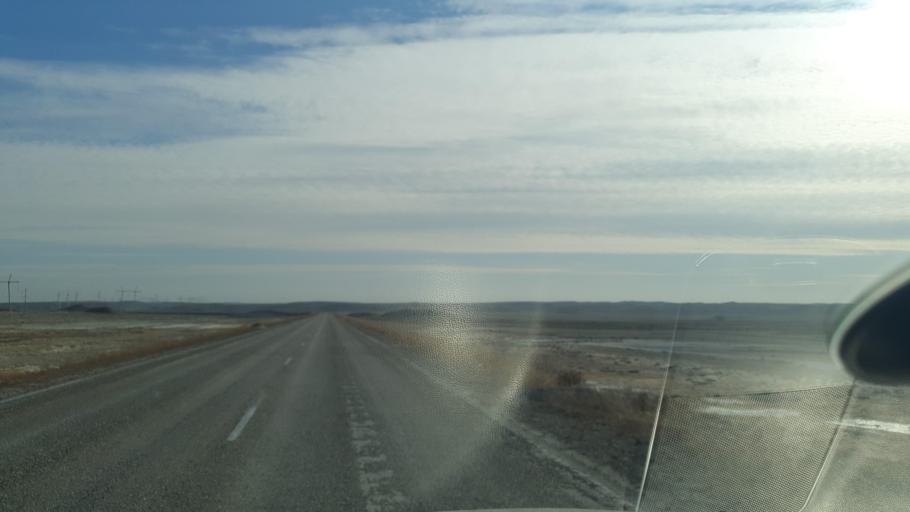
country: KZ
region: Zhambyl
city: Mynaral
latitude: 45.5708
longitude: 73.4168
